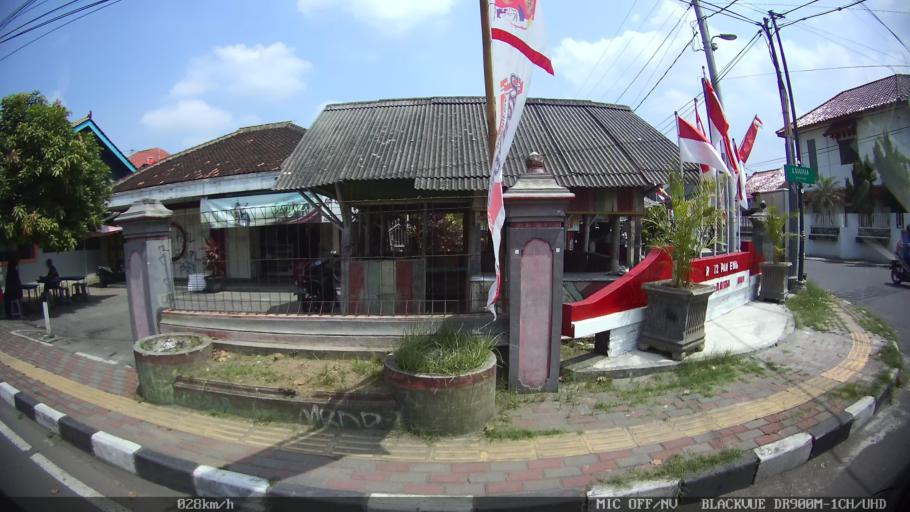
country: ID
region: Daerah Istimewa Yogyakarta
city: Yogyakarta
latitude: -7.8117
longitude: 110.3870
